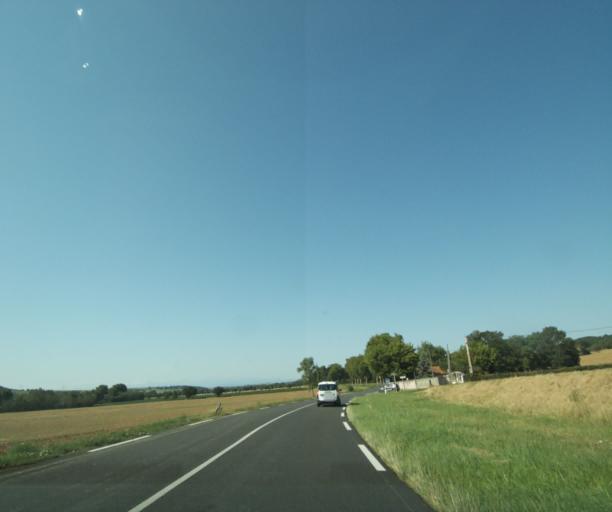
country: FR
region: Midi-Pyrenees
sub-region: Departement de la Haute-Garonne
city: Beaumont-sur-Leze
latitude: 43.3994
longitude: 1.3636
